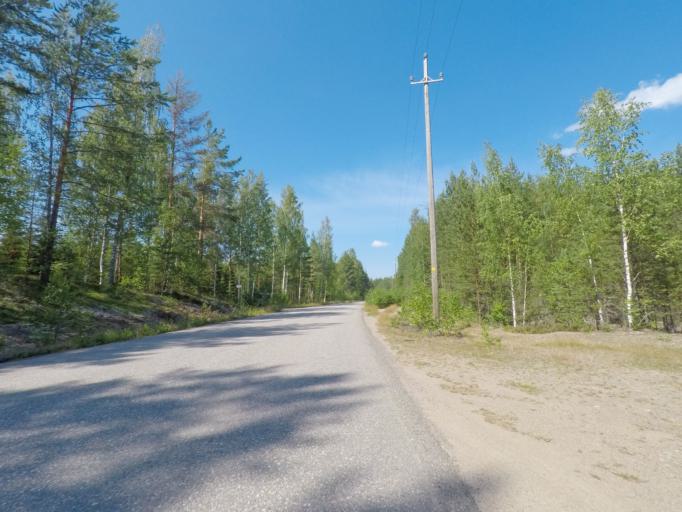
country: FI
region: Southern Savonia
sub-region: Mikkeli
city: Puumala
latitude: 61.4387
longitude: 28.1665
